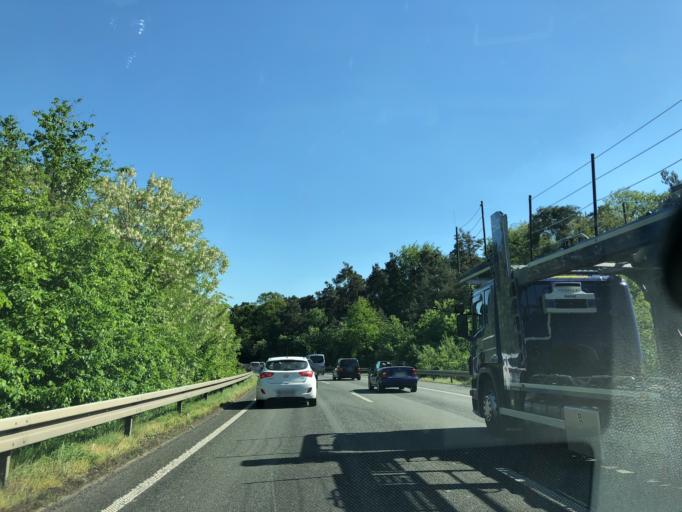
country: DE
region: Hesse
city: Raunheim
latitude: 50.0238
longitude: 8.4918
